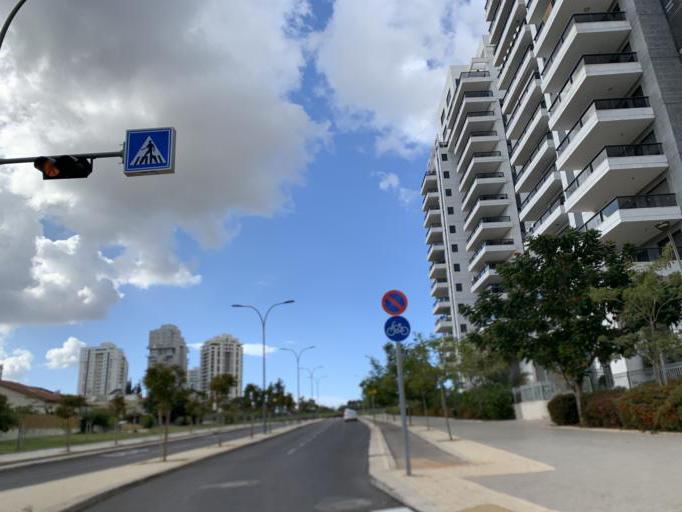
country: IL
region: Central District
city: Hod HaSharon
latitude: 32.1641
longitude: 34.8991
